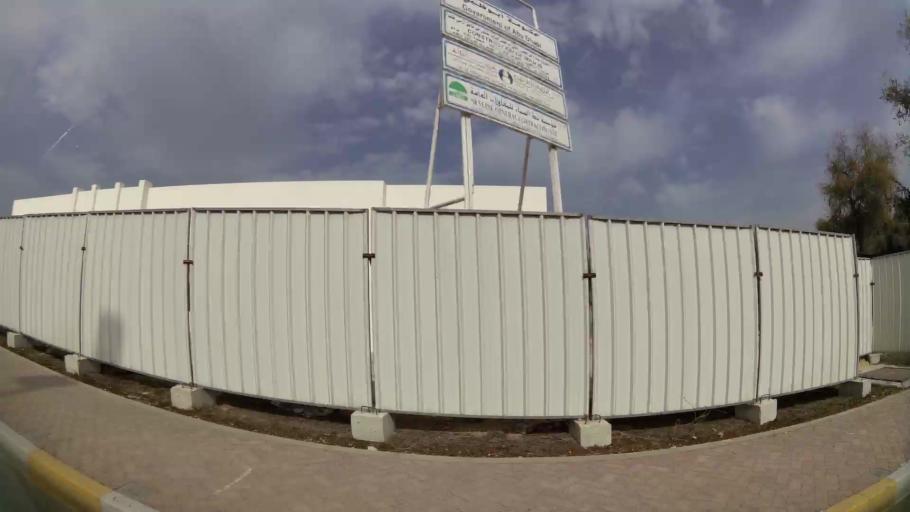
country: AE
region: Abu Dhabi
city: Abu Dhabi
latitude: 24.4521
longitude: 54.3750
